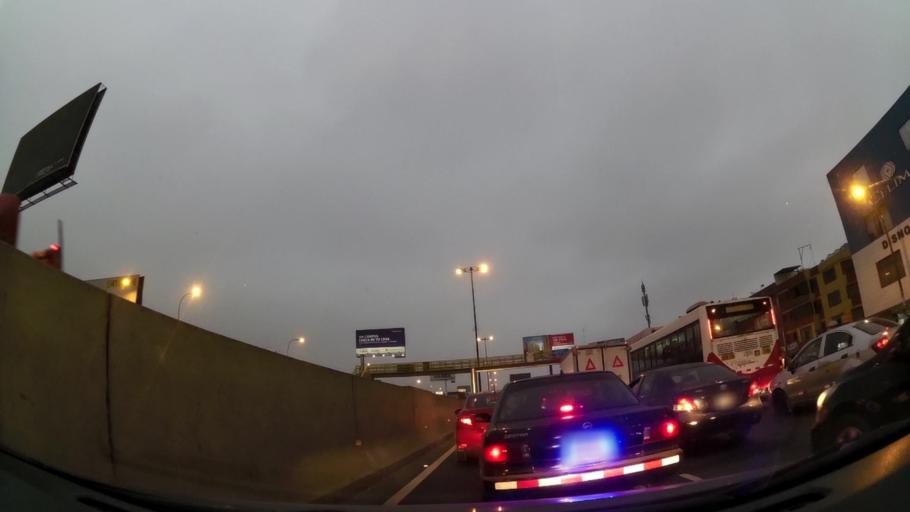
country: PE
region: Lima
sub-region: Lima
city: Independencia
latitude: -12.0204
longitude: -77.0595
